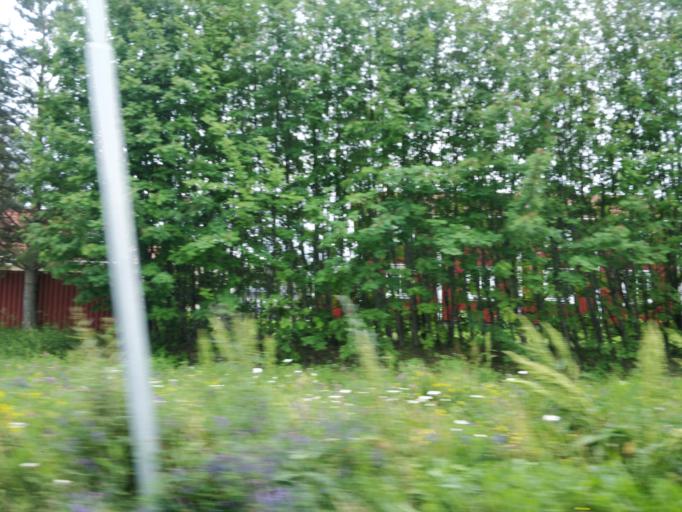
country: SE
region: Vaesterbotten
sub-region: Skelleftea Kommun
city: Viken
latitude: 64.7577
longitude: 20.8951
